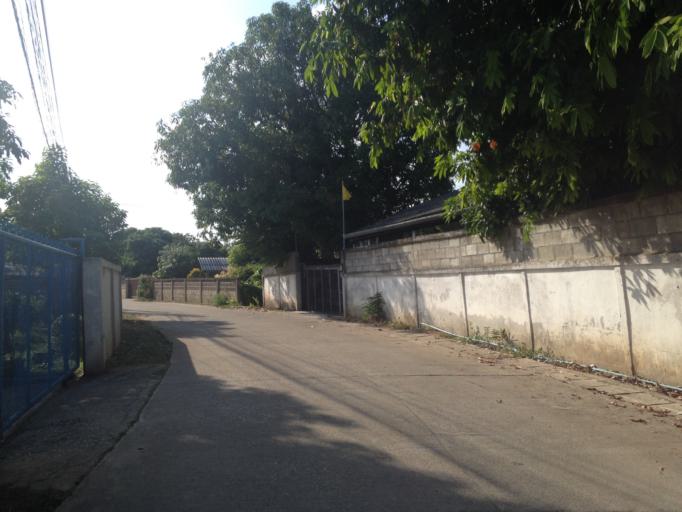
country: TH
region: Chiang Mai
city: Hang Dong
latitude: 18.7061
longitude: 98.9237
